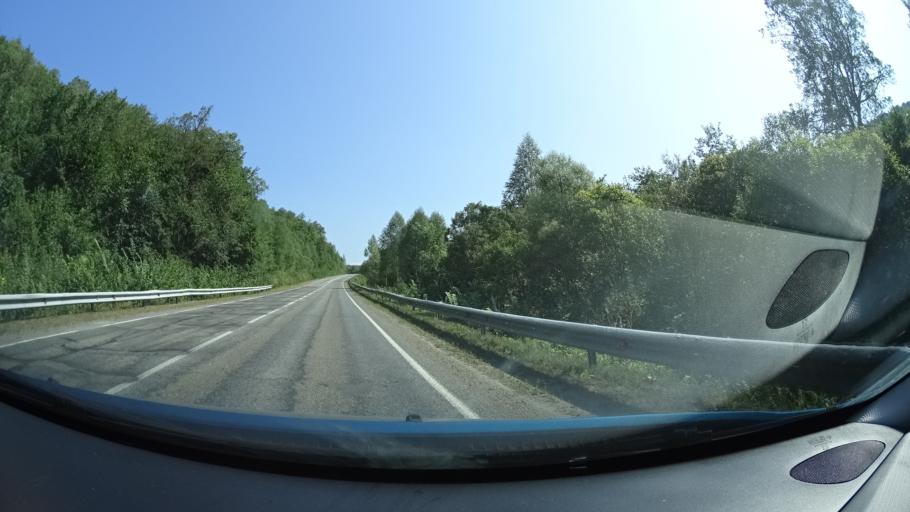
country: RU
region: Bashkortostan
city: Inzer
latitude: 54.3378
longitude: 57.0978
